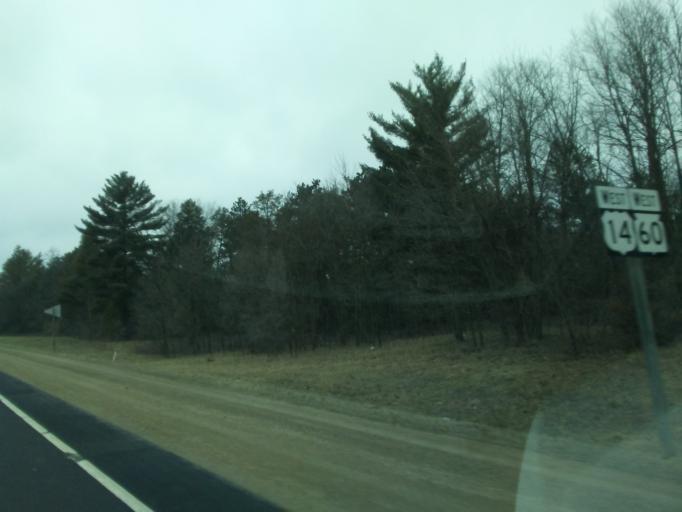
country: US
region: Wisconsin
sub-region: Sauk County
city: Spring Green
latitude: 43.1915
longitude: -90.2136
